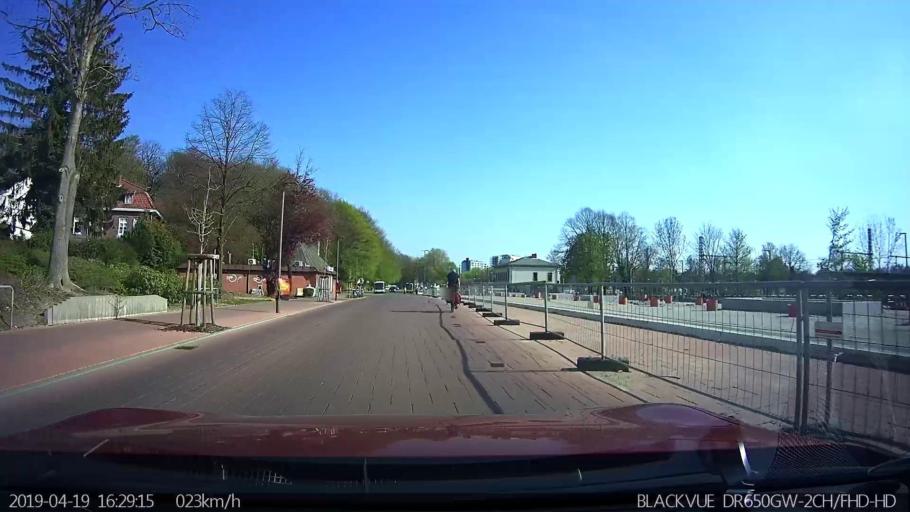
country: DE
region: Schleswig-Holstein
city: Pinneberg
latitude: 53.6565
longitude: 9.7966
